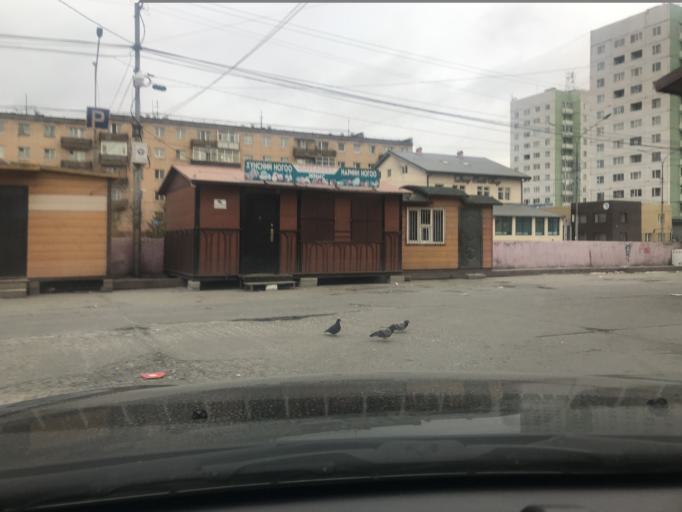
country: MN
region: Ulaanbaatar
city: Ulaanbaatar
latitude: 47.9237
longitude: 106.9397
